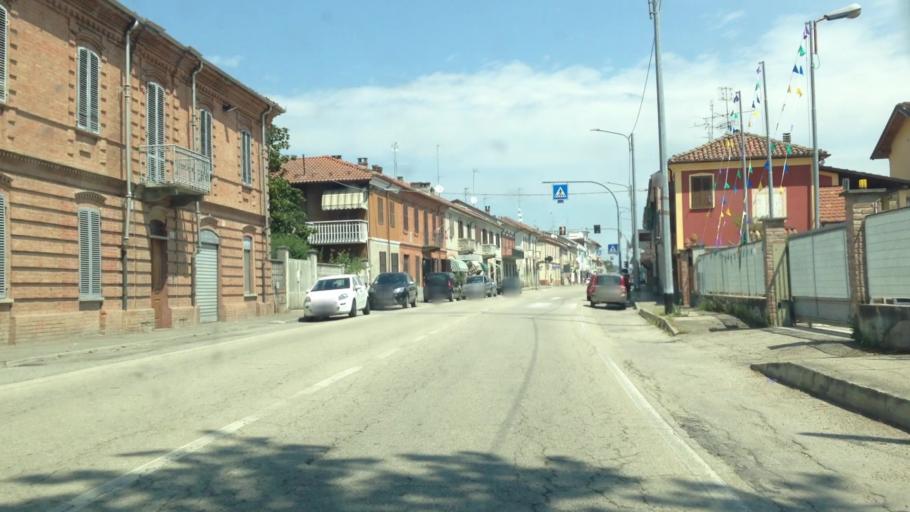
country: IT
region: Piedmont
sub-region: Provincia di Asti
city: Castell'Alfero
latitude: 44.9555
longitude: 8.2230
